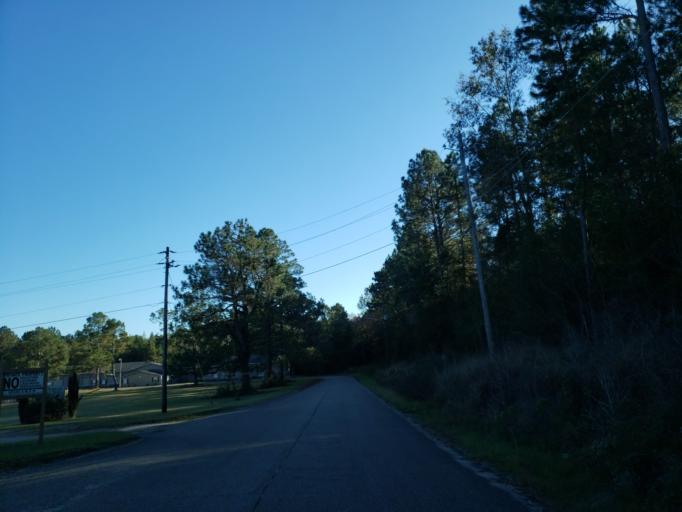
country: US
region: Mississippi
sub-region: Forrest County
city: Hattiesburg
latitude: 31.2758
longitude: -89.2841
